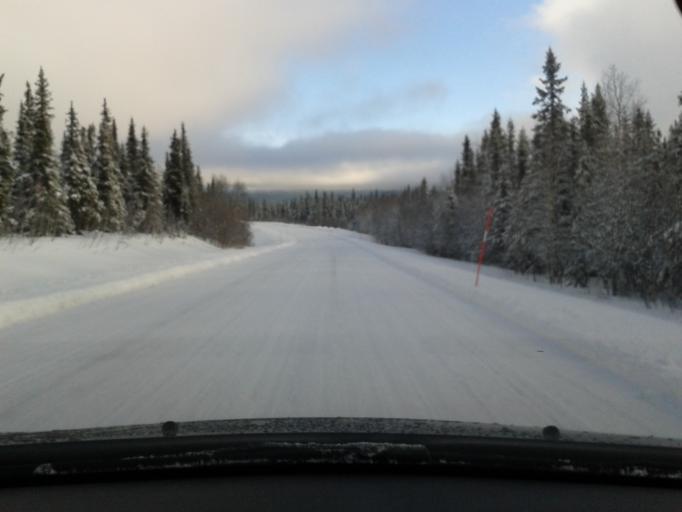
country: SE
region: Vaesterbotten
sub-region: Vilhelmina Kommun
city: Sjoberg
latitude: 65.2518
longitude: 15.6372
